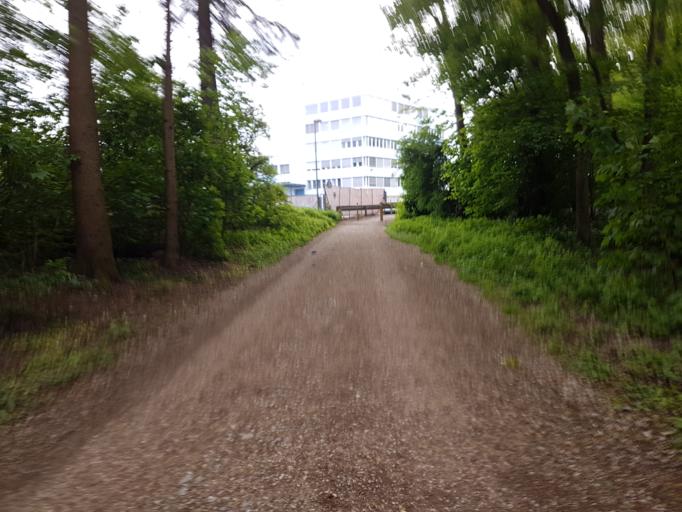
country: CH
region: Solothurn
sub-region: Bezirk Goesgen
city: Niedererlinsbach
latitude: 47.3830
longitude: 8.0101
